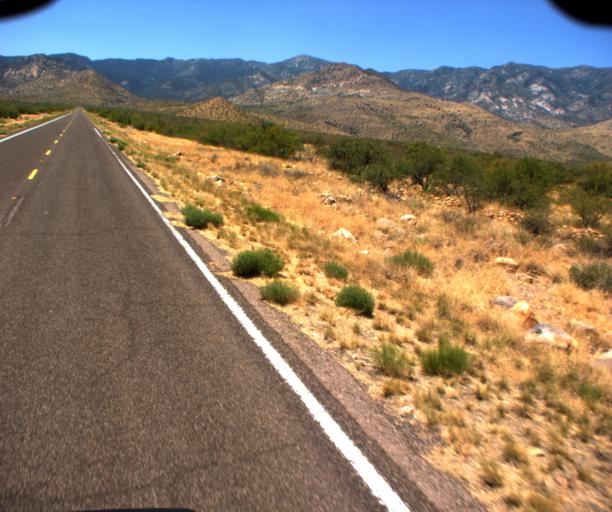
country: US
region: Arizona
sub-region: Graham County
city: Swift Trail Junction
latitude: 32.7033
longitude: -109.7410
